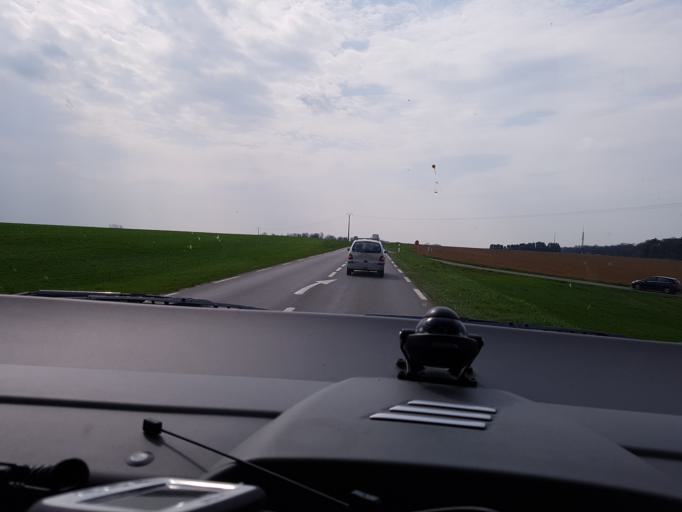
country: FR
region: Picardie
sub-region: Departement de l'Aisne
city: Crouy
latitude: 49.4151
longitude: 3.3434
